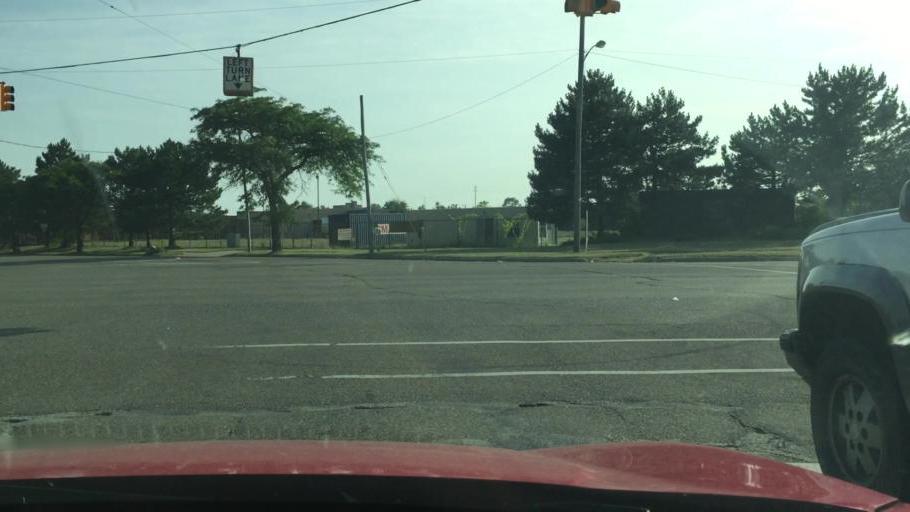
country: US
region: Michigan
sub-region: Genesee County
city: Flint
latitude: 43.0349
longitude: -83.6827
